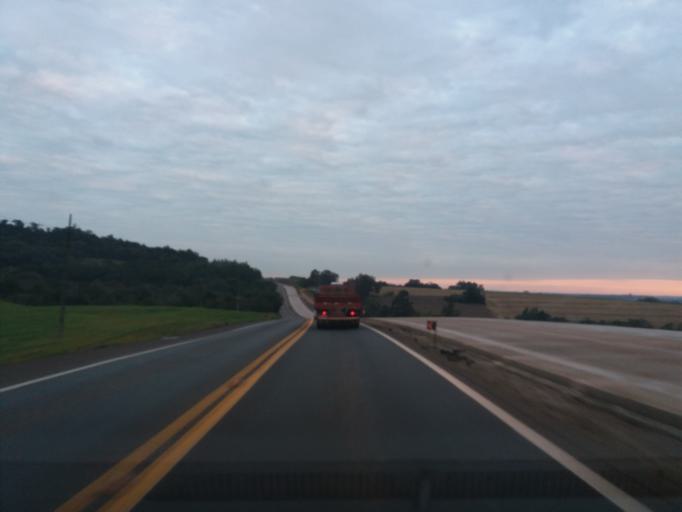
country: BR
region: Parana
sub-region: Realeza
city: Realeza
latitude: -25.3934
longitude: -53.5766
